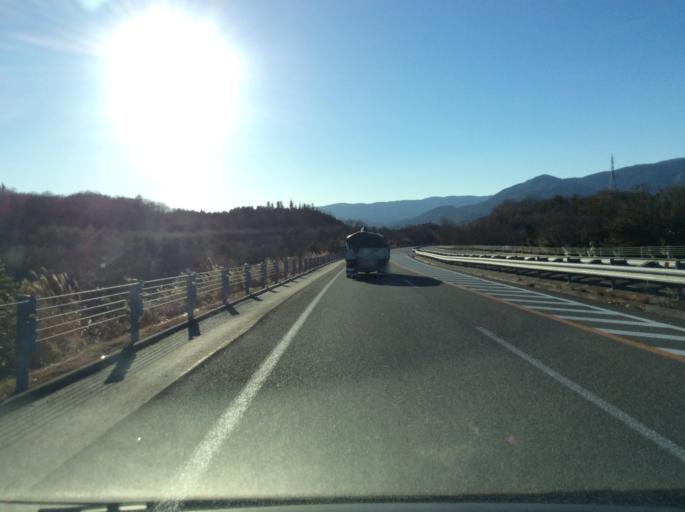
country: JP
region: Fukushima
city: Iwaki
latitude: 37.1080
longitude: 140.8878
